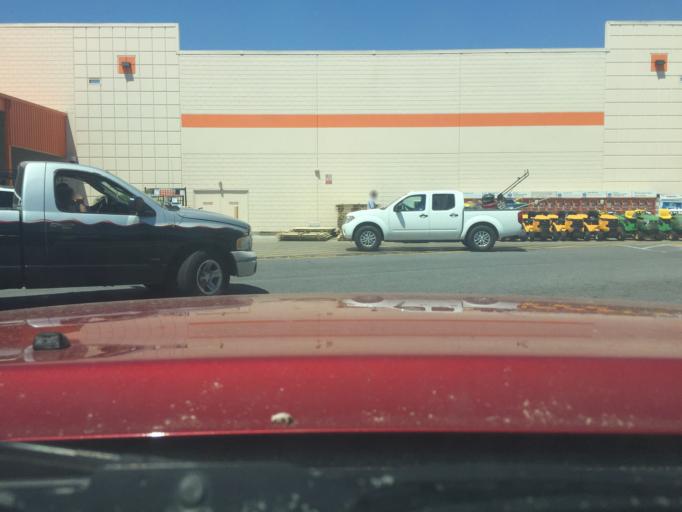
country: US
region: Georgia
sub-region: Chatham County
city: Thunderbolt
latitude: 32.0417
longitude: -81.0678
